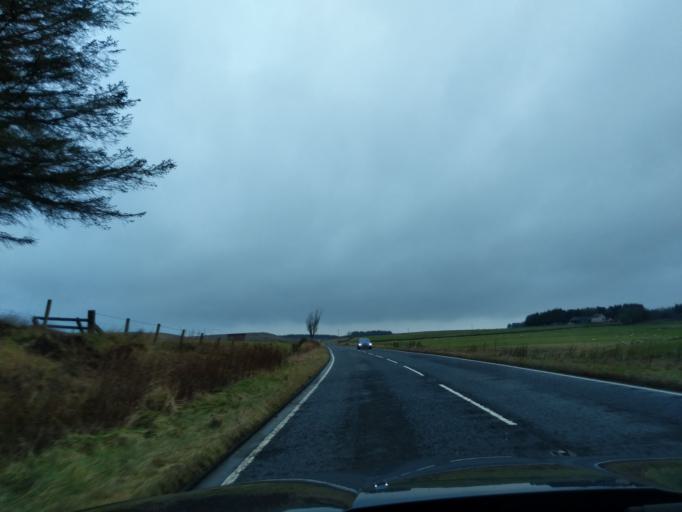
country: GB
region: England
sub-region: Northumberland
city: Corsenside
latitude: 55.1916
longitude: -2.0608
